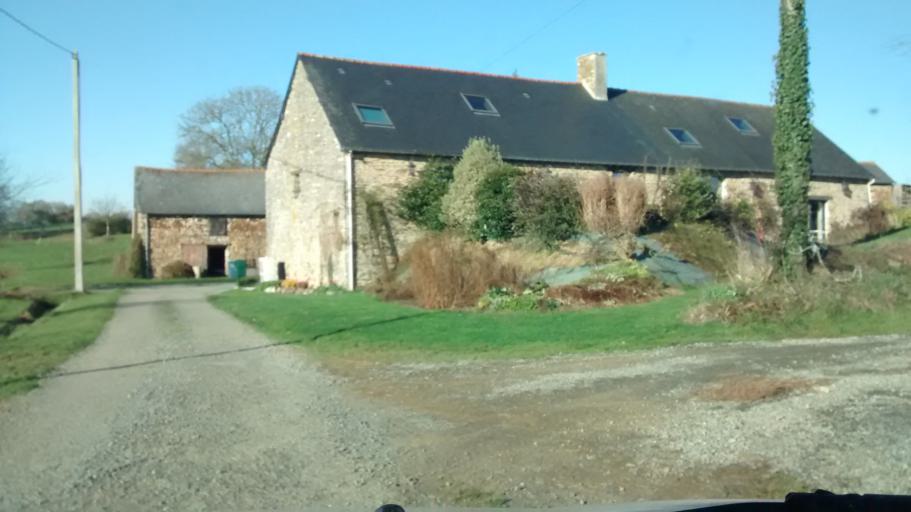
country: FR
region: Brittany
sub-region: Departement d'Ille-et-Vilaine
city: Gosne
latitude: 48.2085
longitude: -1.4689
